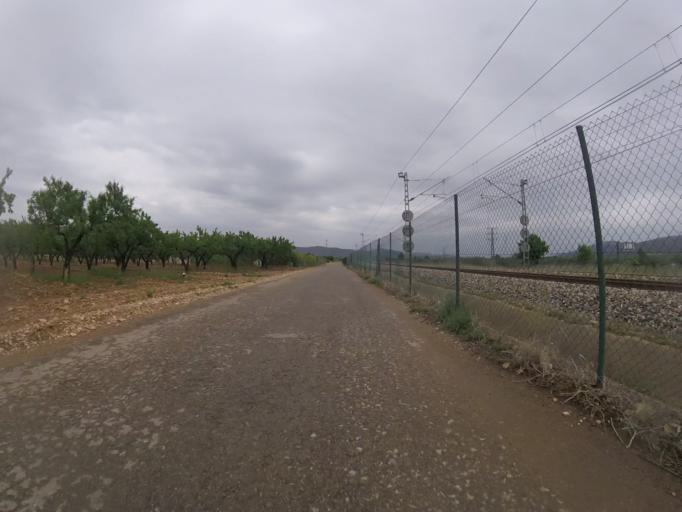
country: ES
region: Valencia
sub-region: Provincia de Castello
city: Alcala de Xivert
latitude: 40.3155
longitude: 0.2330
